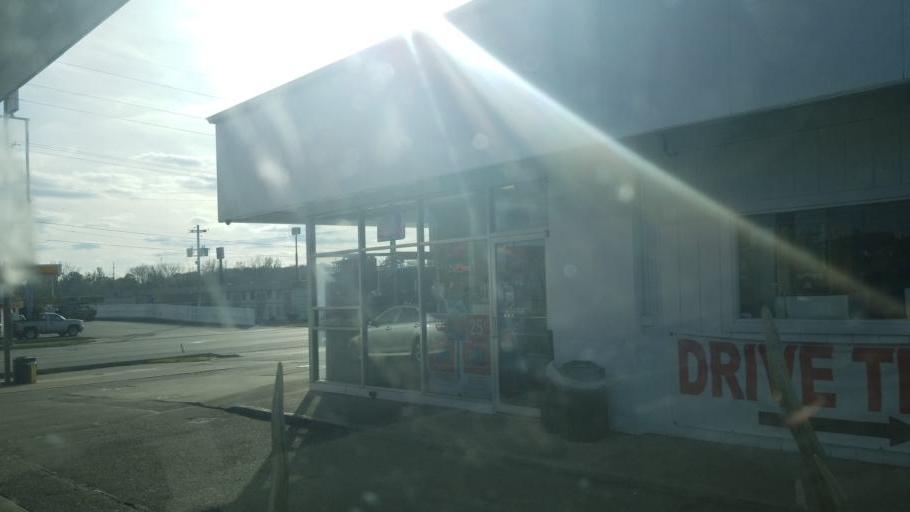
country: US
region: Ohio
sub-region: Clark County
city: Springfield
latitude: 39.8952
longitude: -83.8118
